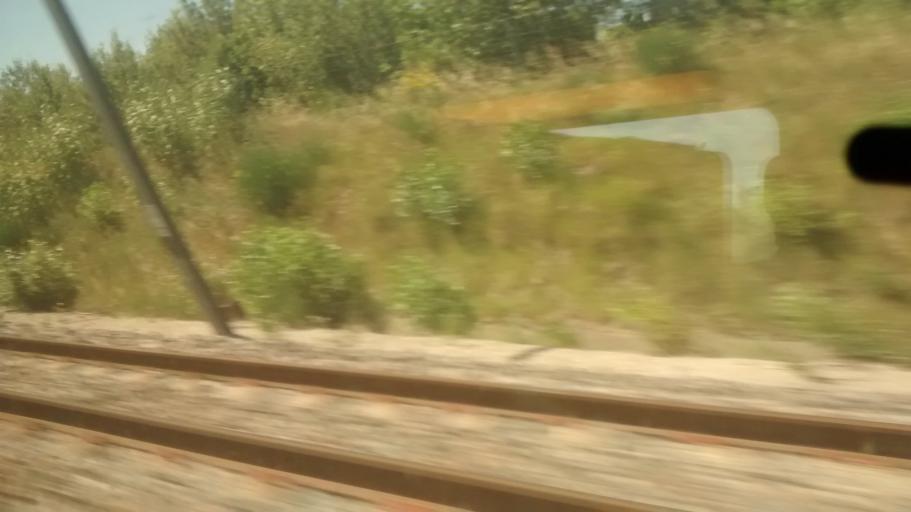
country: FR
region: Rhone-Alpes
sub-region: Departement de la Drome
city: Pierrelatte
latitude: 44.3667
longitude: 4.7232
